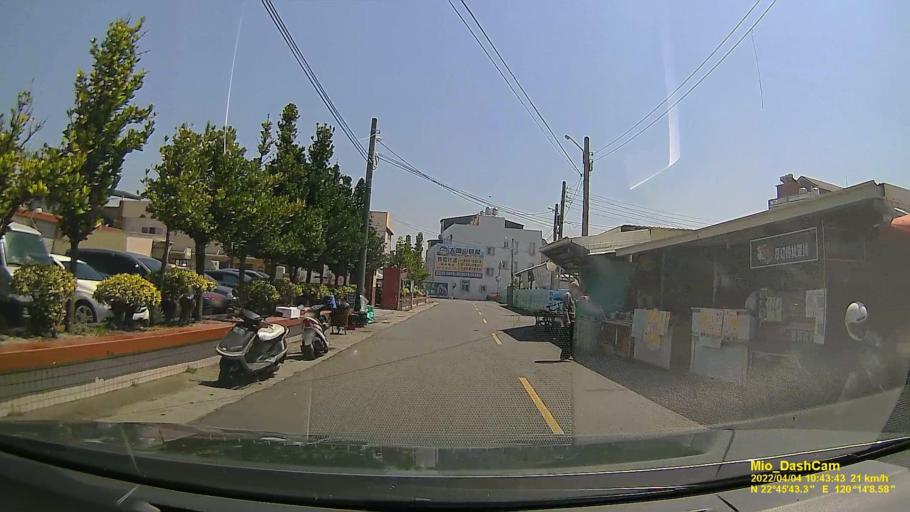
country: TW
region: Kaohsiung
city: Kaohsiung
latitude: 22.7620
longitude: 120.2357
